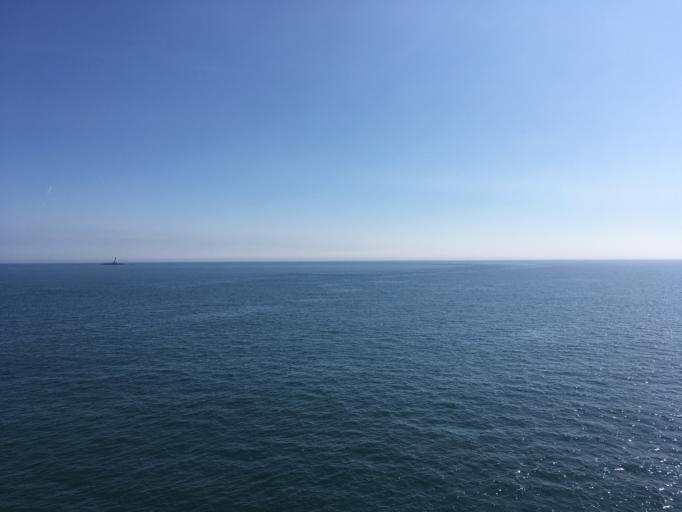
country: IE
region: Leinster
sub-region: Loch Garman
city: Ballygerry
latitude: 52.2319
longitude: -6.2135
